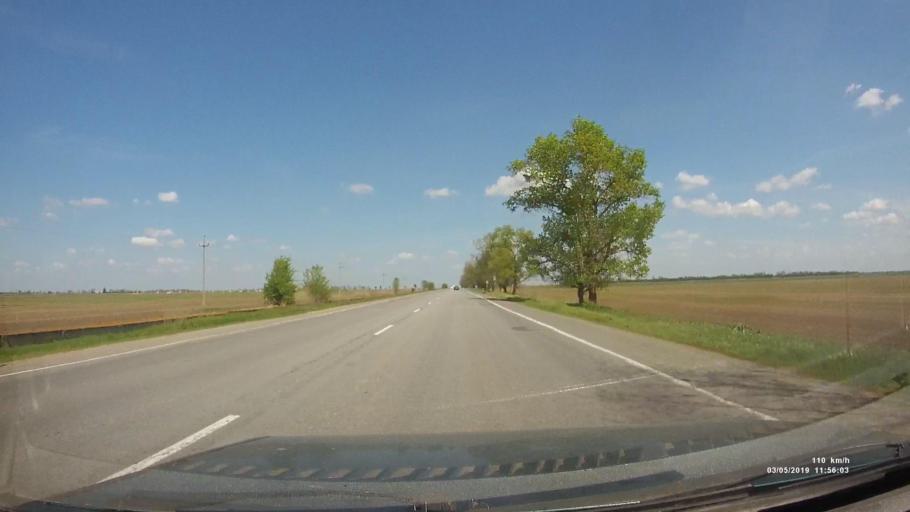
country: RU
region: Rostov
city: Bagayevskaya
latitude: 47.1893
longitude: 40.2971
